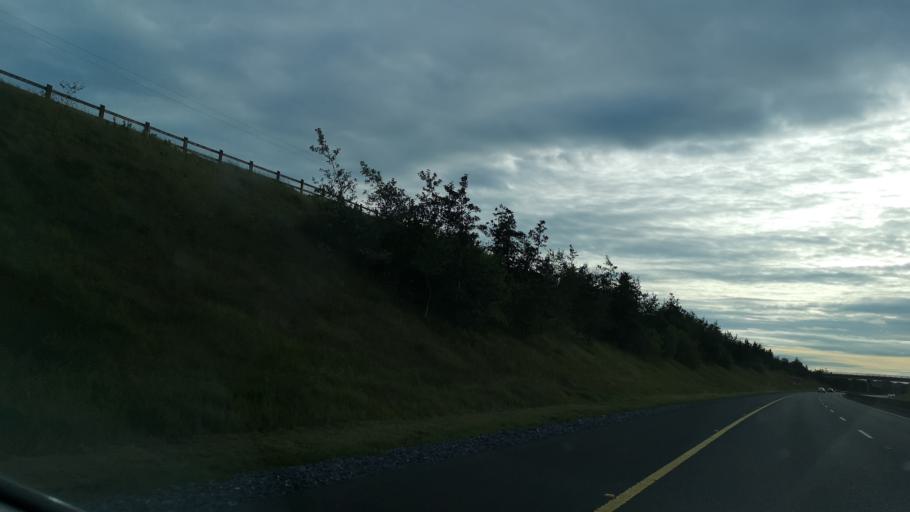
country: IE
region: Connaught
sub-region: County Galway
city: Loughrea
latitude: 53.2789
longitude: -8.5226
